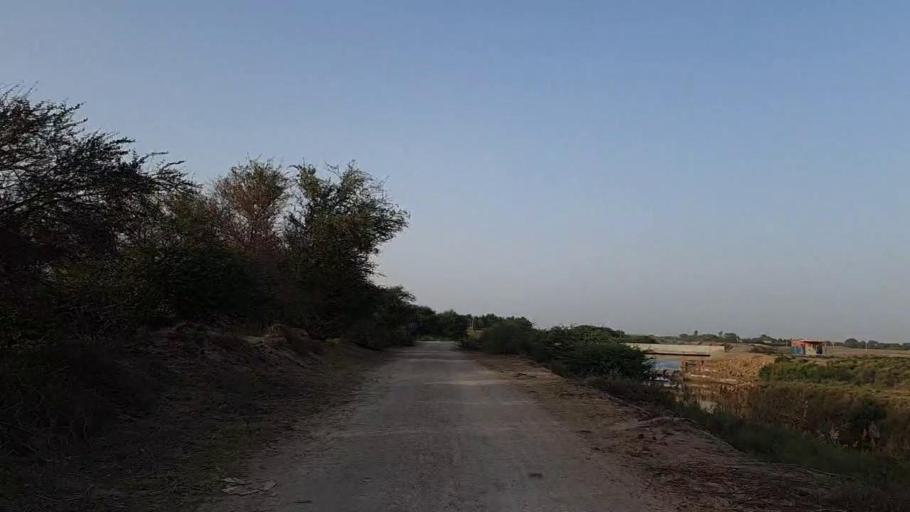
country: PK
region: Sindh
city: Jati
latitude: 24.4141
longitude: 68.1865
